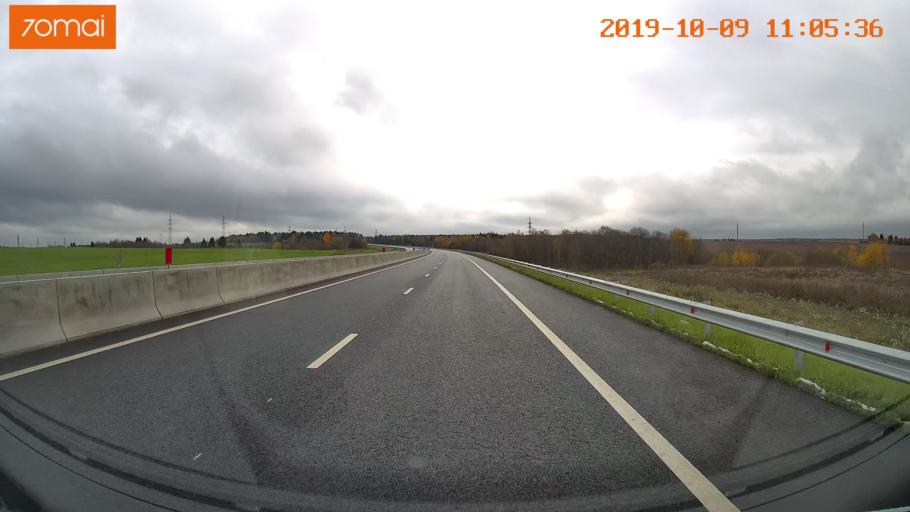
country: RU
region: Vologda
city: Molochnoye
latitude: 59.1977
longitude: 39.7581
